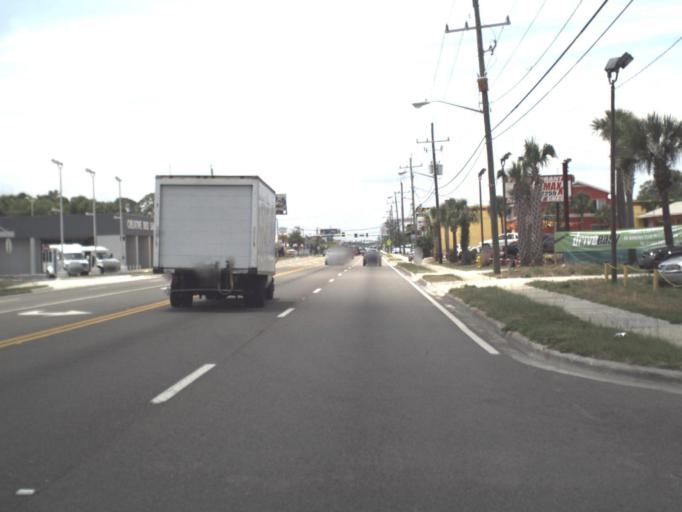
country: US
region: Florida
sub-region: Duval County
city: Jacksonville
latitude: 30.3143
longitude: -81.5657
